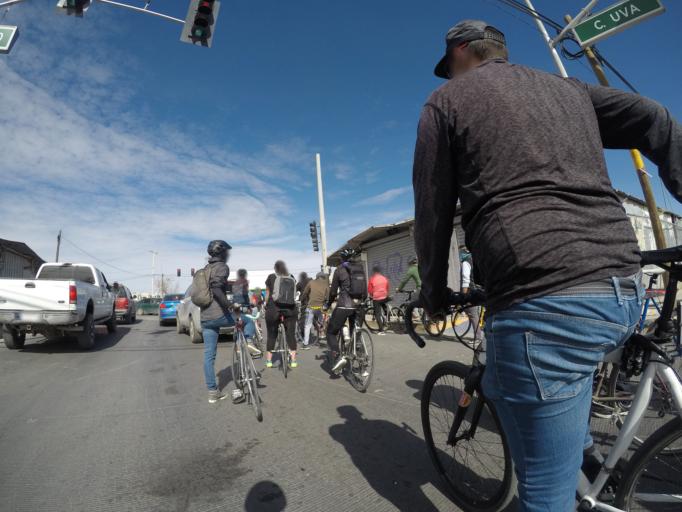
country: US
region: Texas
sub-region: El Paso County
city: Socorro
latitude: 31.6653
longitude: -106.4010
